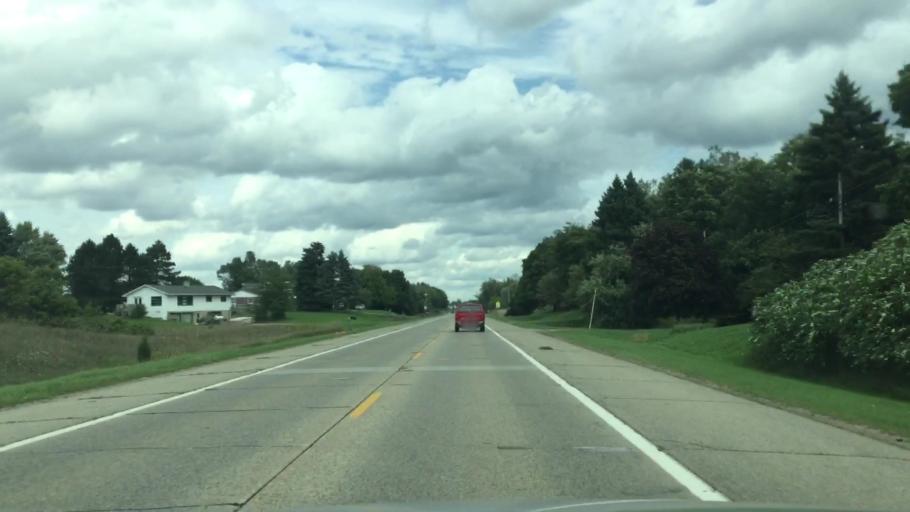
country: US
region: Michigan
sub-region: Shiawassee County
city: Owosso
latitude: 42.9617
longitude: -84.2024
